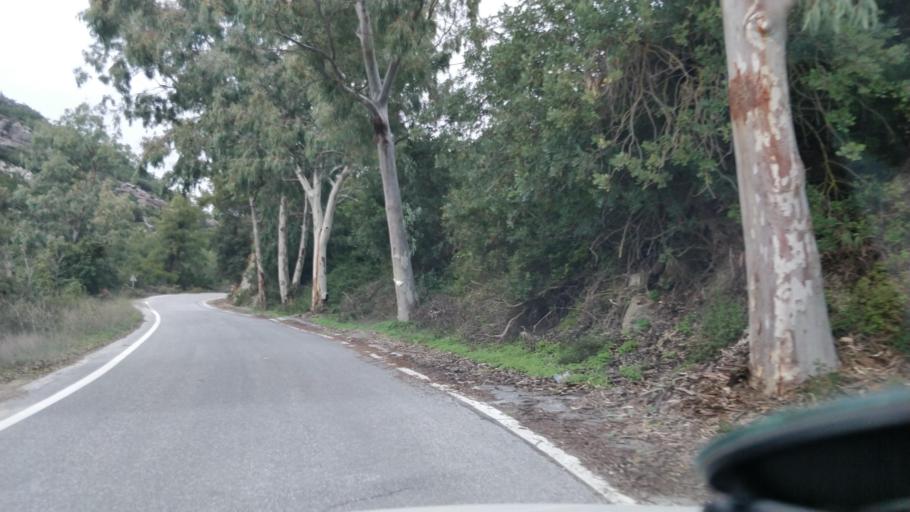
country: GR
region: Crete
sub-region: Nomos Lasithiou
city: Gra Liyia
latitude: 35.0959
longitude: 25.6983
